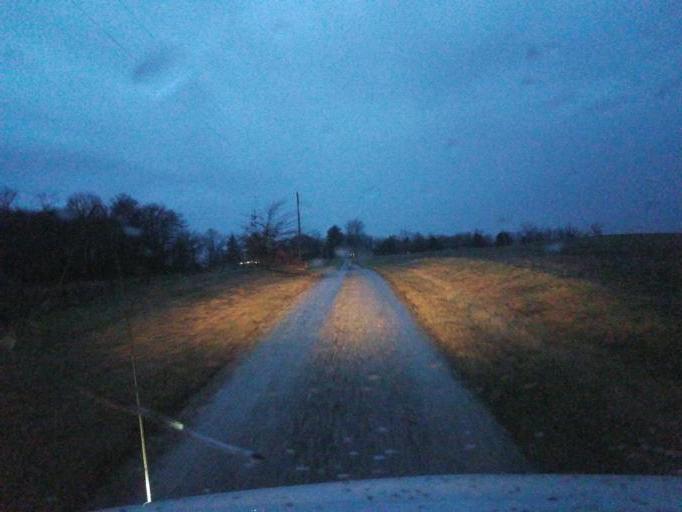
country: US
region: Ohio
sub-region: Knox County
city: Gambier
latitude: 40.3188
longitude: -82.4488
